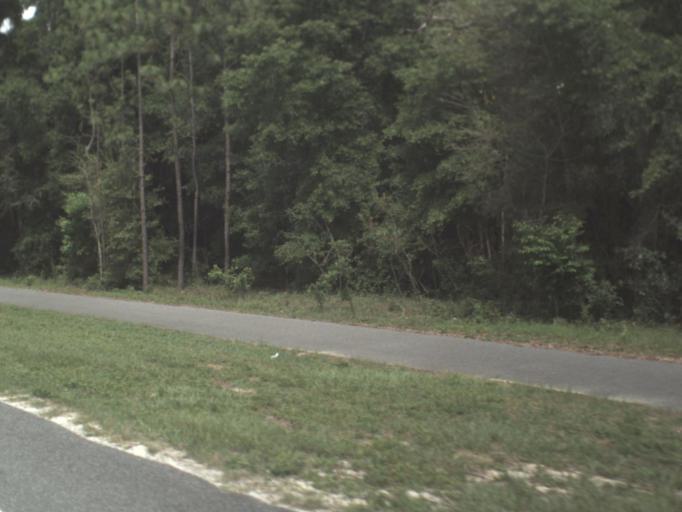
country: US
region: Florida
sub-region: Clay County
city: Keystone Heights
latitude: 29.8469
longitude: -81.9634
